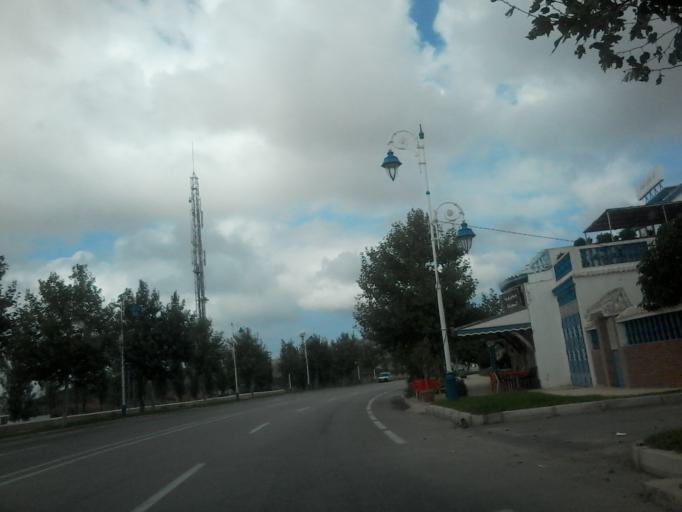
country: MA
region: Tanger-Tetouan
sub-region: Tetouan
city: Martil
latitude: 35.6423
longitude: -5.2932
